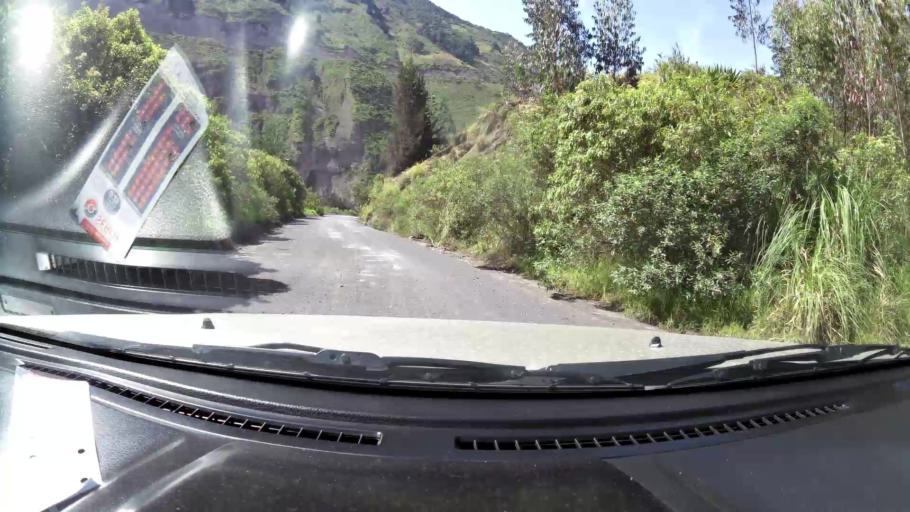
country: EC
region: Tungurahua
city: Banos
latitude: -1.4823
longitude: -78.5125
